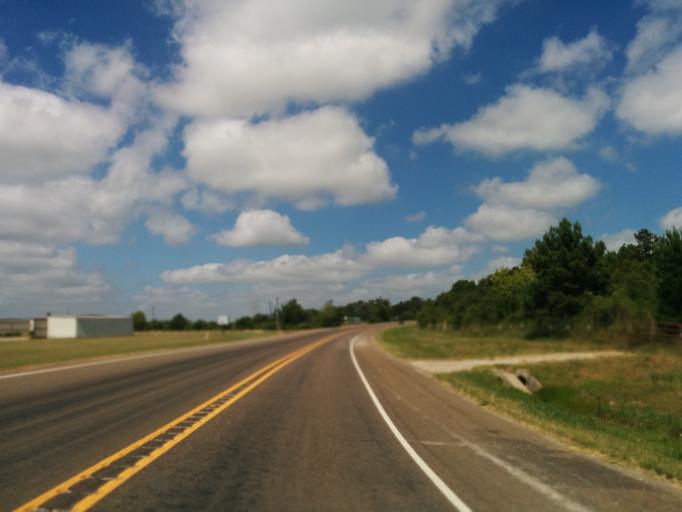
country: US
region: Texas
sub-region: Houston County
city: Crockett
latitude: 31.3143
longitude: -95.4012
